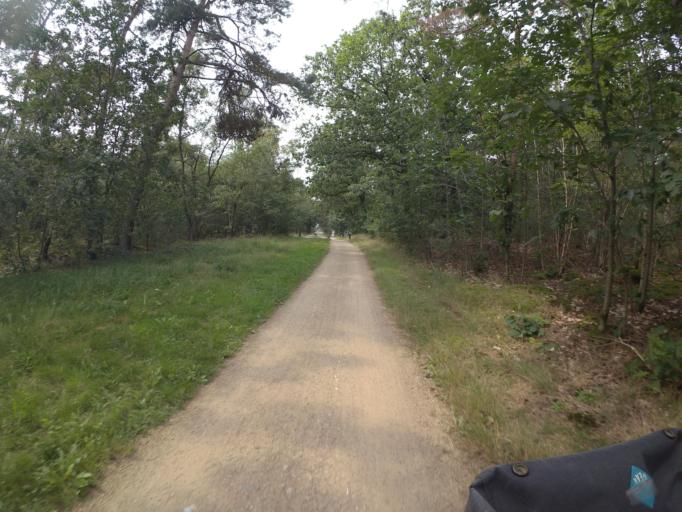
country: NL
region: Limburg
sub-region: Gemeente Bergen
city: Wellerlooi
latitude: 51.5883
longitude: 6.1162
